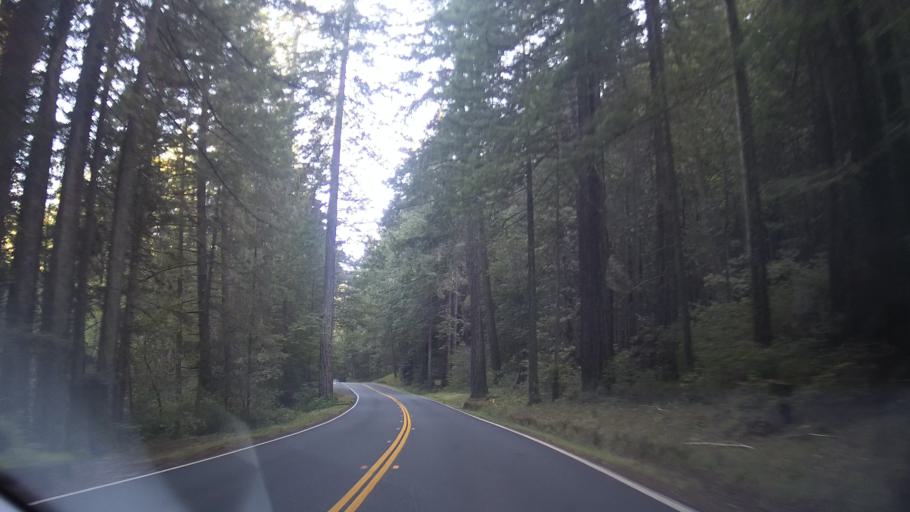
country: US
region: California
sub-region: Mendocino County
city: Brooktrails
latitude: 39.3504
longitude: -123.5623
